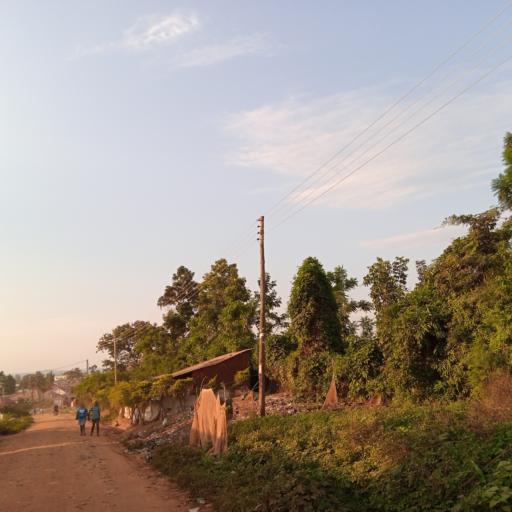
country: UG
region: Eastern Region
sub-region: Mbale District
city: Mbale
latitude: 1.0820
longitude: 34.1663
